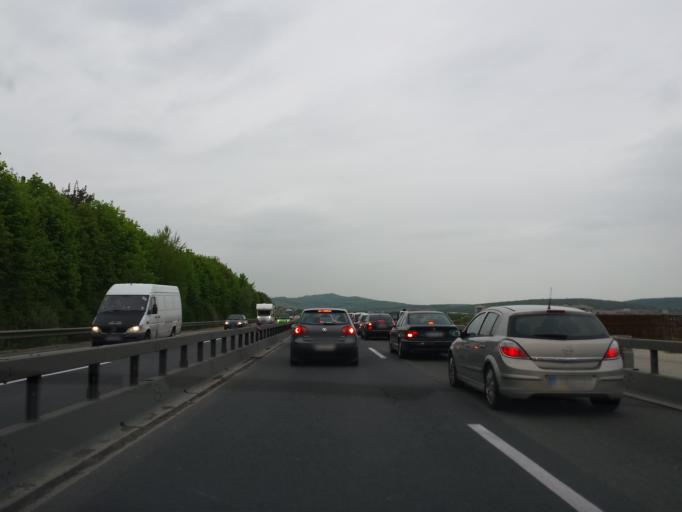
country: HU
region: Pest
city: Toeroekbalint
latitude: 47.4509
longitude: 18.8867
